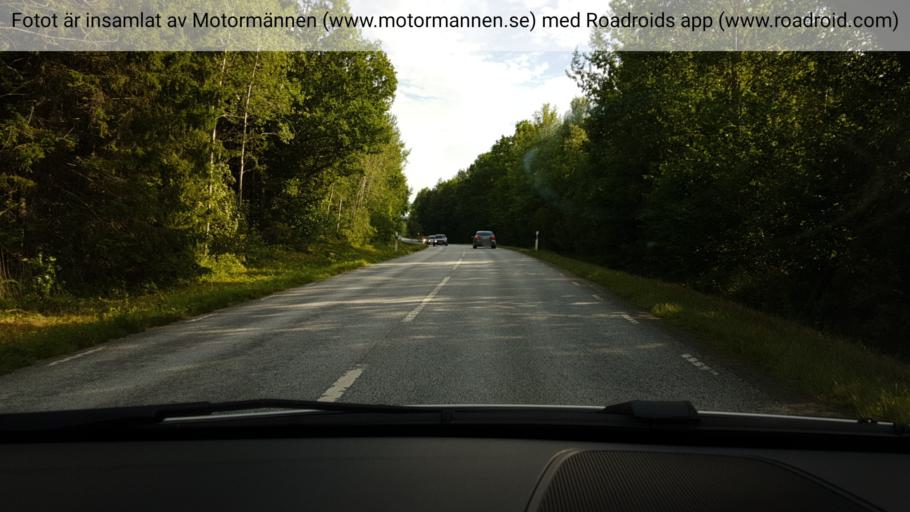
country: SE
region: Stockholm
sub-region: Norrtalje Kommun
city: Hallstavik
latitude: 59.9269
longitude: 18.7092
